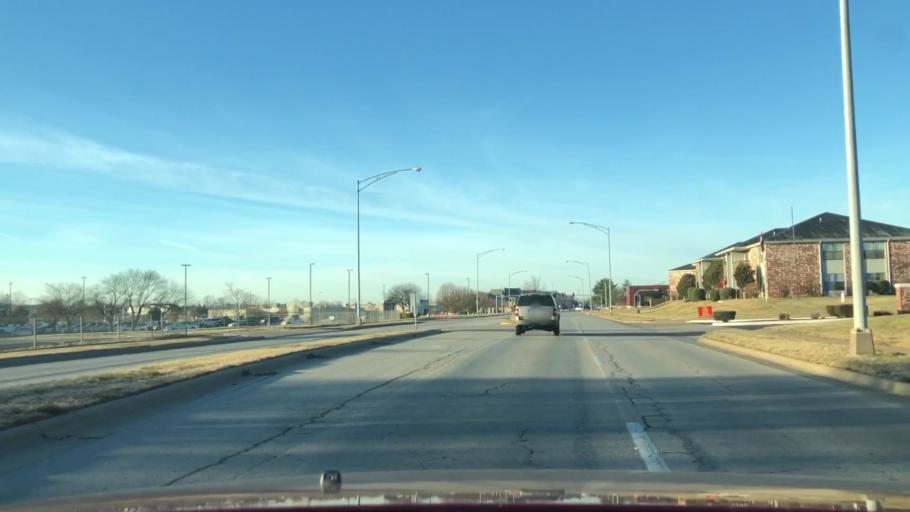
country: US
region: Missouri
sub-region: Greene County
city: Springfield
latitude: 37.1492
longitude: -93.2635
